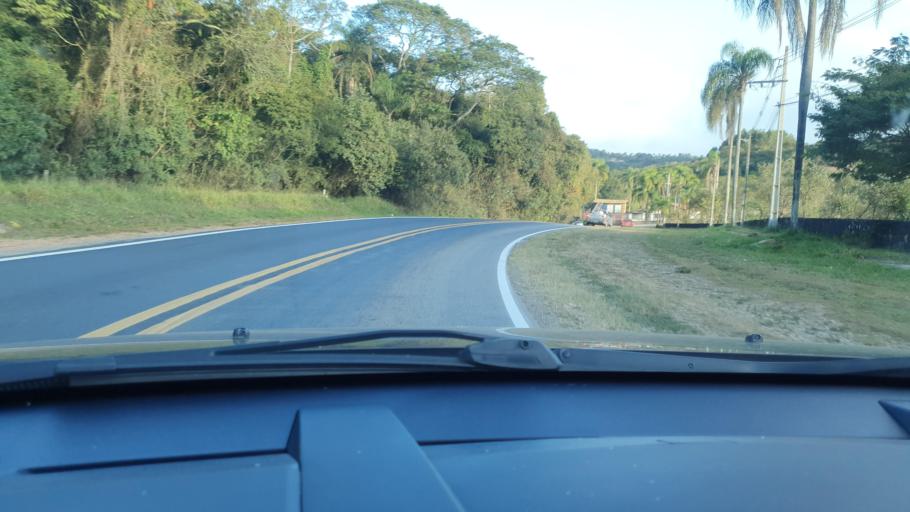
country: BR
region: Sao Paulo
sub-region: Ibiuna
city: Ibiuna
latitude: -23.6765
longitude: -47.3069
